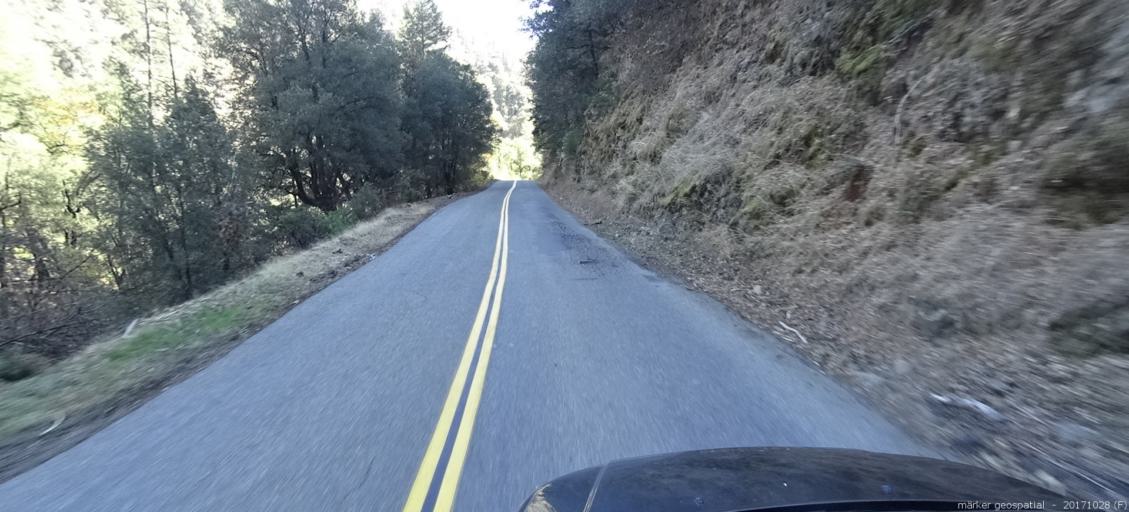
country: US
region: California
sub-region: Trinity County
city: Lewiston
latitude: 40.7736
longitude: -122.6128
